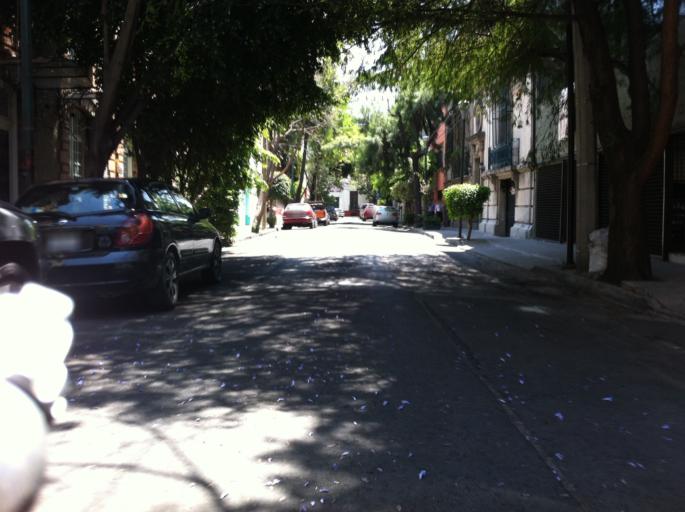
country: MX
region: Mexico City
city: Benito Juarez
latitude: 19.4216
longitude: -99.1630
